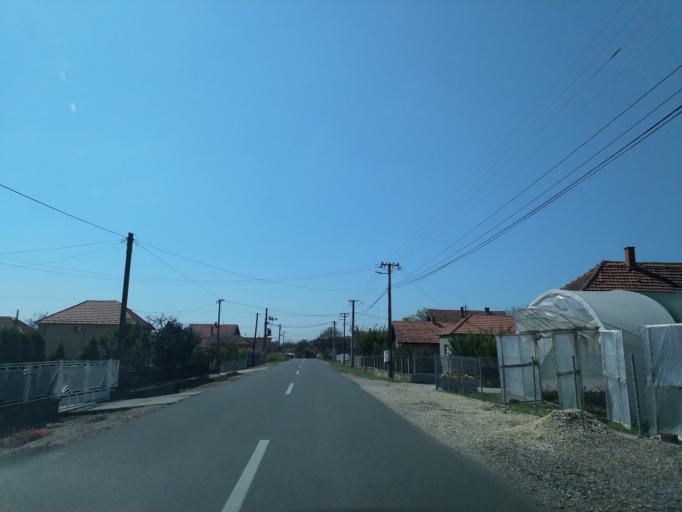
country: RS
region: Central Serbia
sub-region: Rasinski Okrug
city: Krusevac
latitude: 43.6194
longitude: 21.3061
